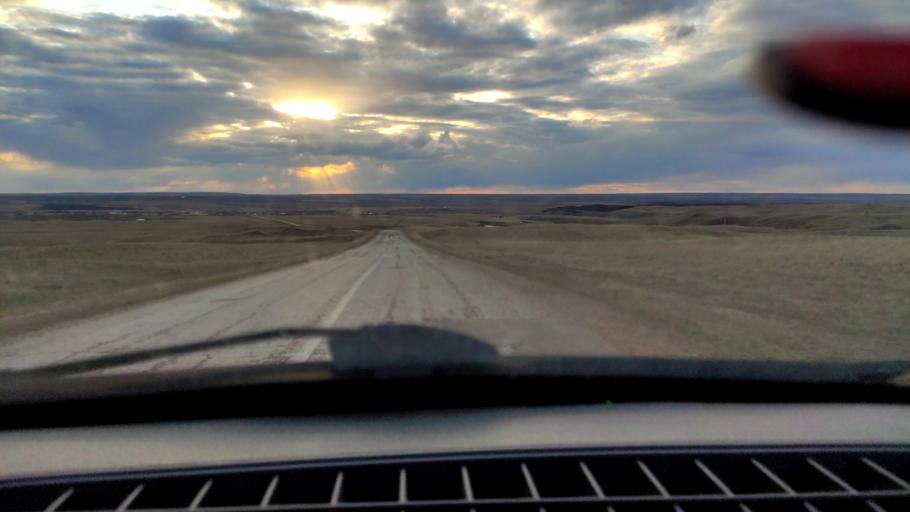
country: RU
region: Bashkortostan
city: Tolbazy
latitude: 54.0122
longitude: 55.5682
